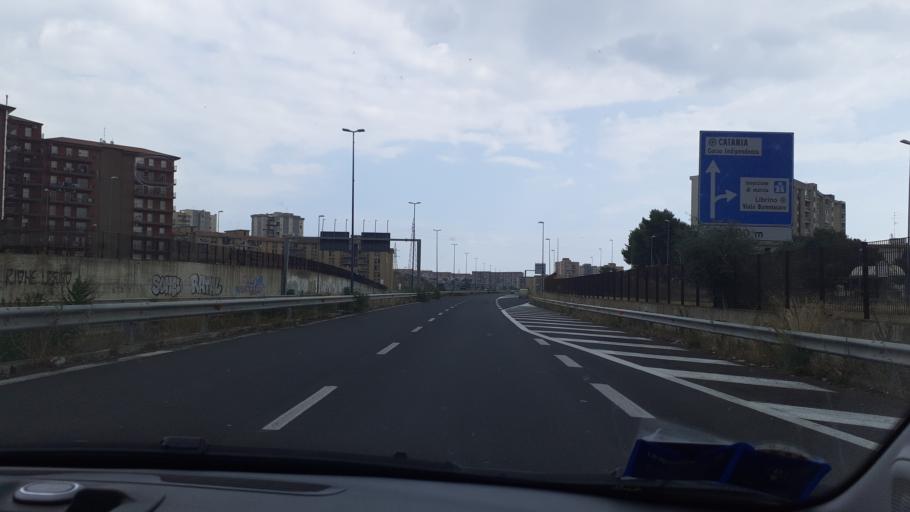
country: IT
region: Sicily
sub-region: Catania
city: Catania
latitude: 37.4802
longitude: 15.0489
